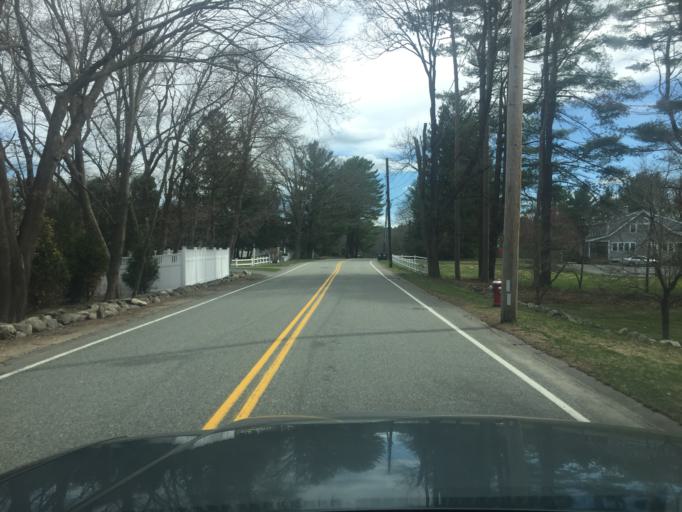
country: US
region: Massachusetts
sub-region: Norfolk County
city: Medfield
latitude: 42.2131
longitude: -71.3165
